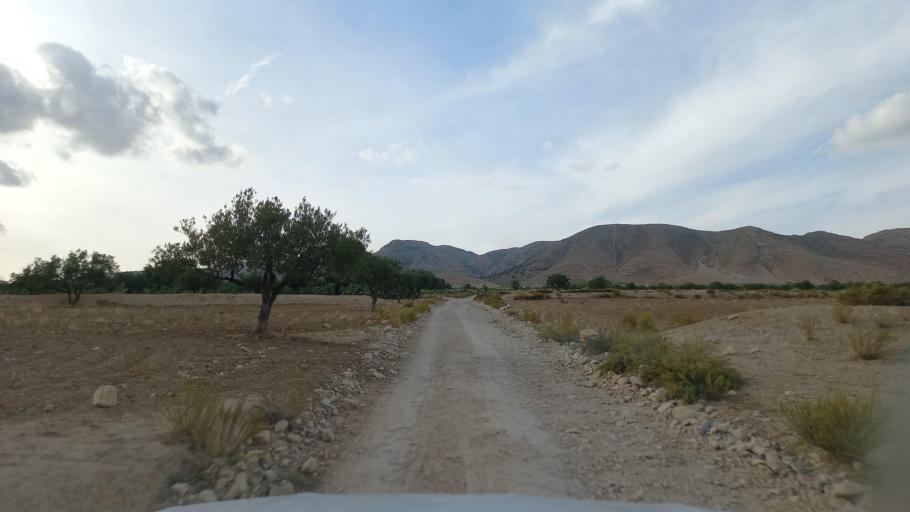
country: TN
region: Al Qasrayn
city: Sbiba
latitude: 35.4431
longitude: 9.0724
